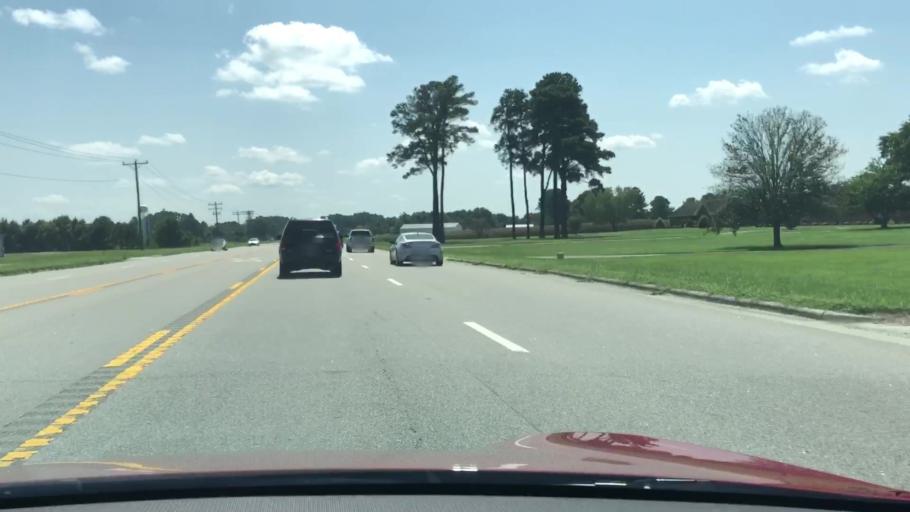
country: US
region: North Carolina
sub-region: Currituck County
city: Moyock
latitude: 36.5373
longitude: -76.1863
